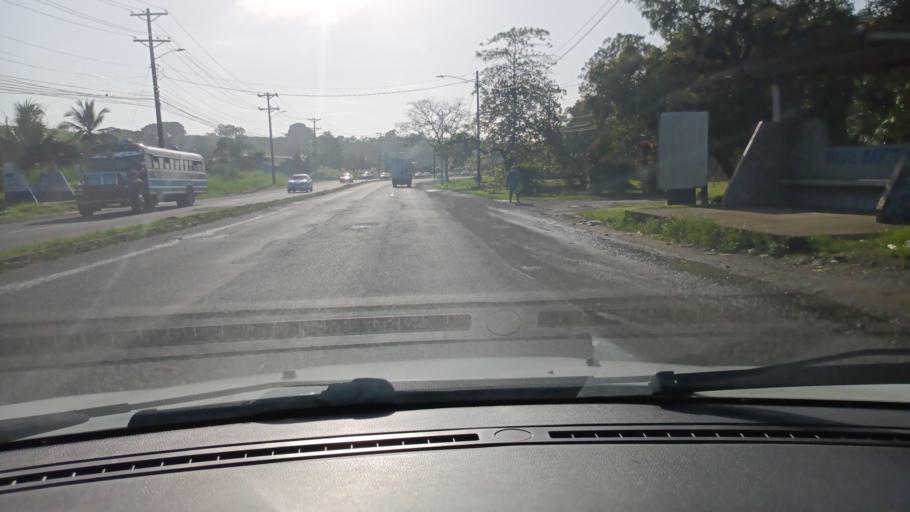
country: PA
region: Colon
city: Sabanitas
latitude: 9.3581
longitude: -79.8179
